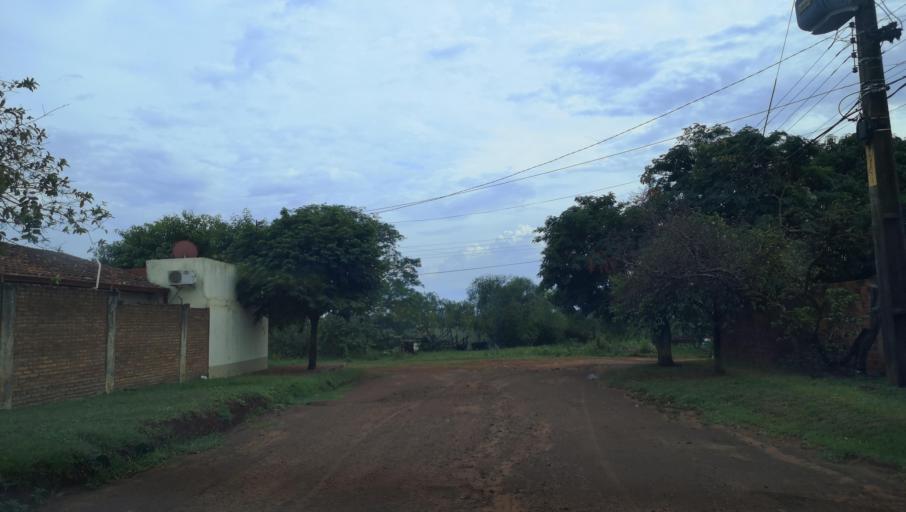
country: PY
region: Misiones
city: Santa Maria
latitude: -26.8823
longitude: -57.0400
